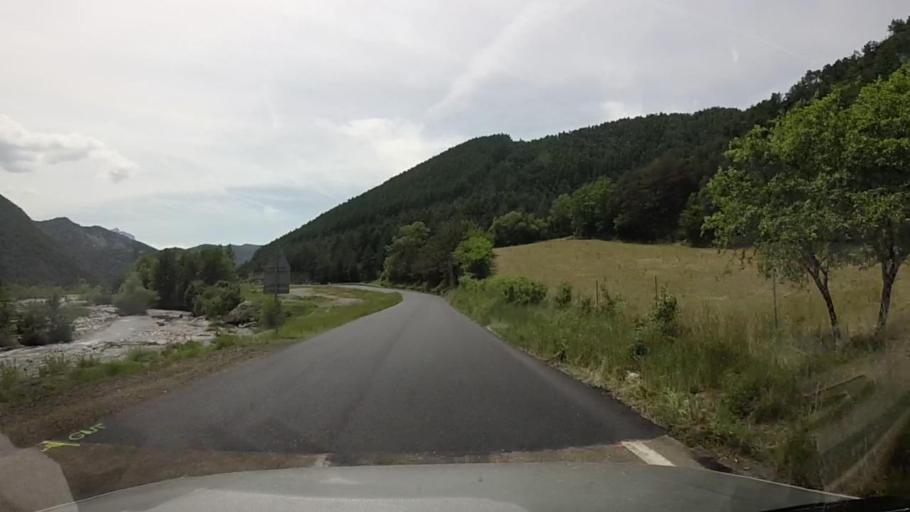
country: FR
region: Provence-Alpes-Cote d'Azur
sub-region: Departement des Alpes-de-Haute-Provence
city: Le Brusquet
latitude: 44.1954
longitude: 6.3682
